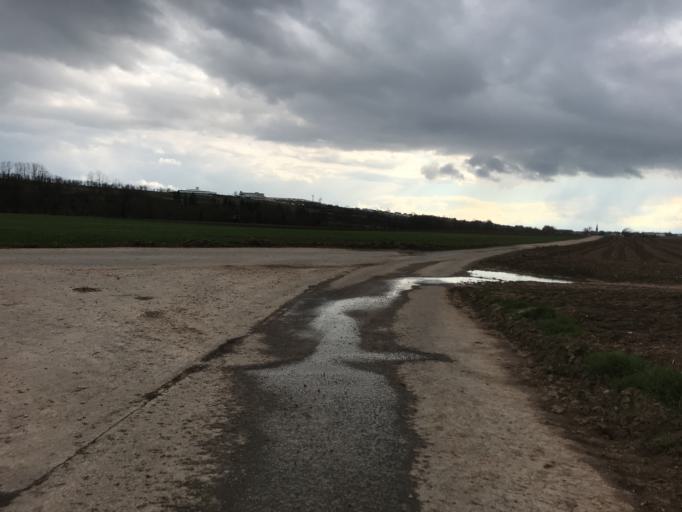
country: DE
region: Rheinland-Pfalz
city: Udenheim
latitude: 49.8915
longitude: 8.1745
